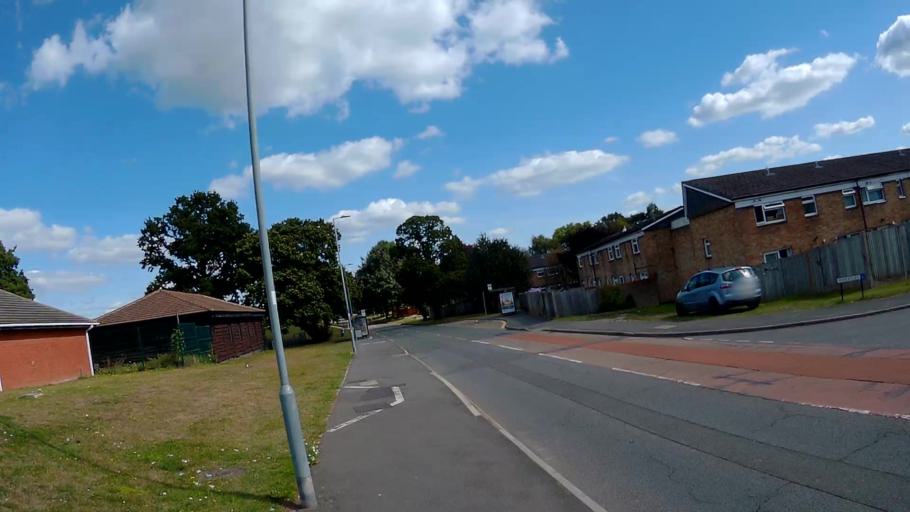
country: GB
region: England
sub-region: Bracknell Forest
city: Bracknell
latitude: 51.4033
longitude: -0.7758
